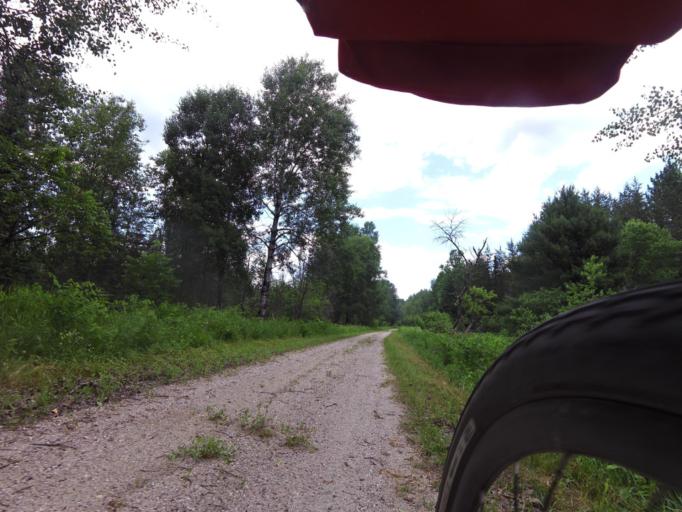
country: CA
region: Quebec
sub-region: Outaouais
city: Maniwaki
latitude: 46.0289
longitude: -76.0982
